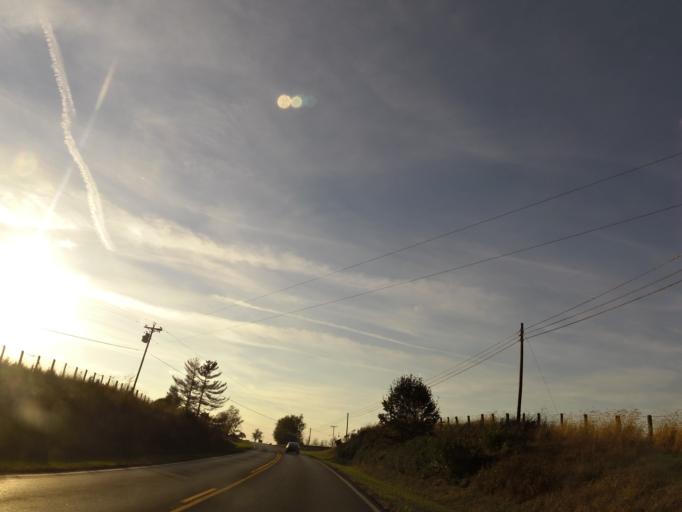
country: US
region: Kentucky
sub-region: Garrard County
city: Lancaster
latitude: 37.6679
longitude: -84.6261
